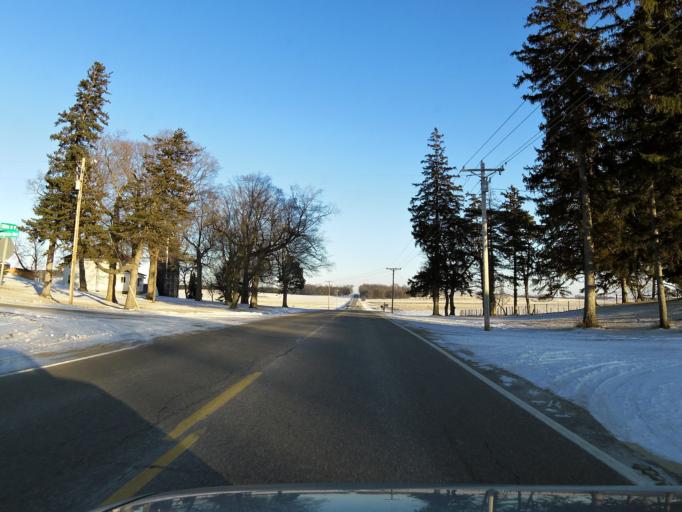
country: US
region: Minnesota
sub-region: Rice County
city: Northfield
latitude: 44.5438
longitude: -93.1878
